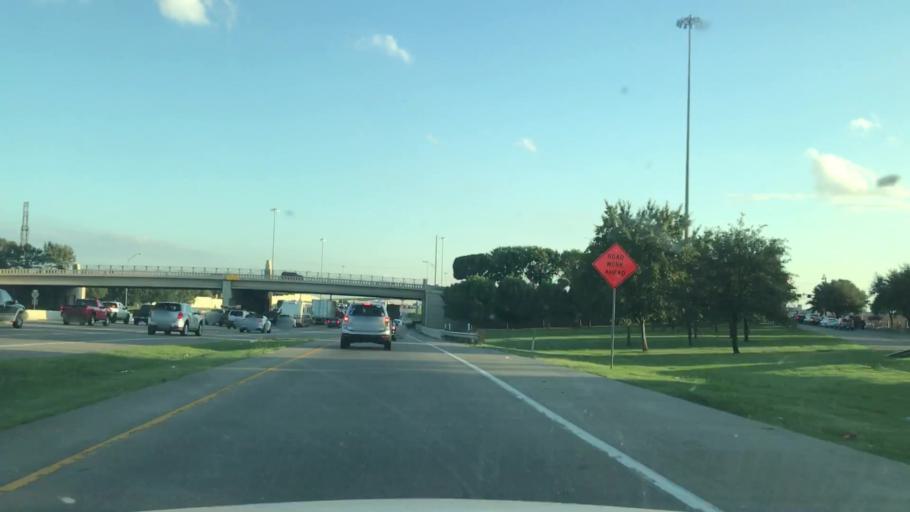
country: US
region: Texas
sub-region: Dallas County
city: Mesquite
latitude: 32.8035
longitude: -96.6271
